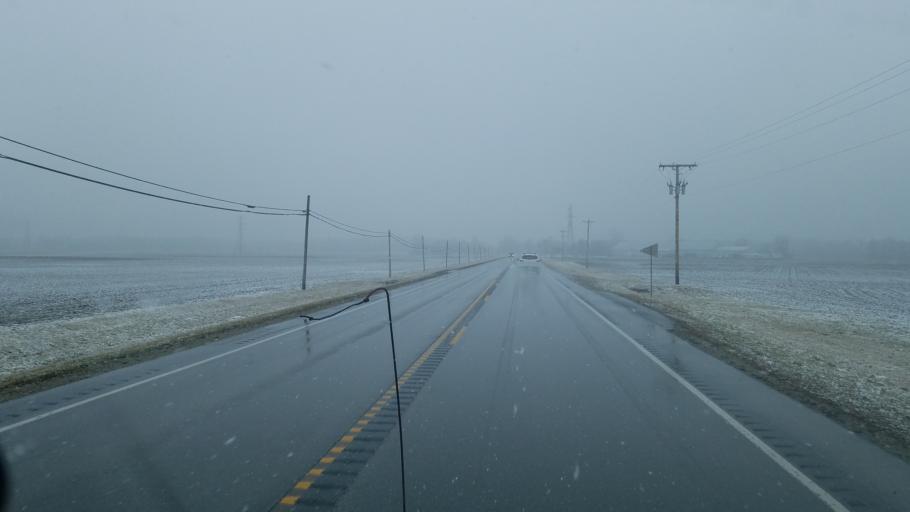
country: US
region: Indiana
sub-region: Grant County
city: Marion
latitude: 40.6242
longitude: -85.7007
